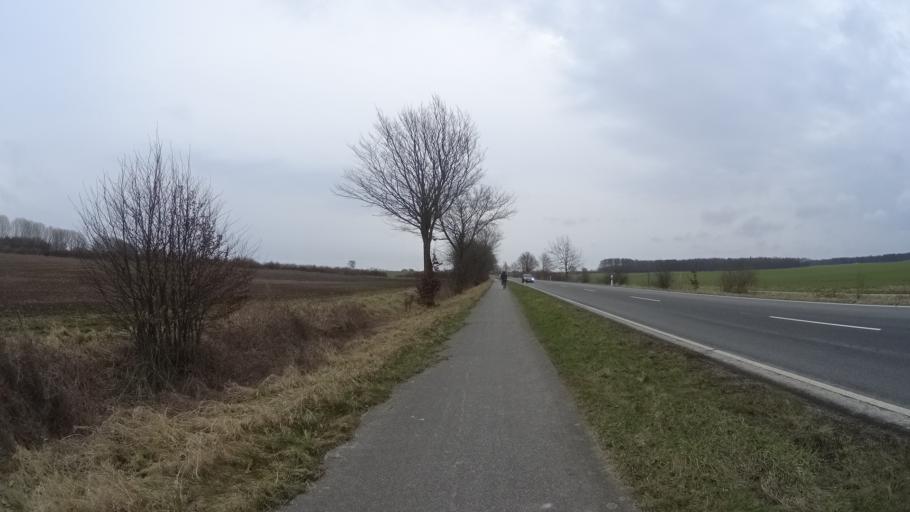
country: DE
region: Schleswig-Holstein
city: Stakendorf
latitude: 54.3826
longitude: 10.4450
